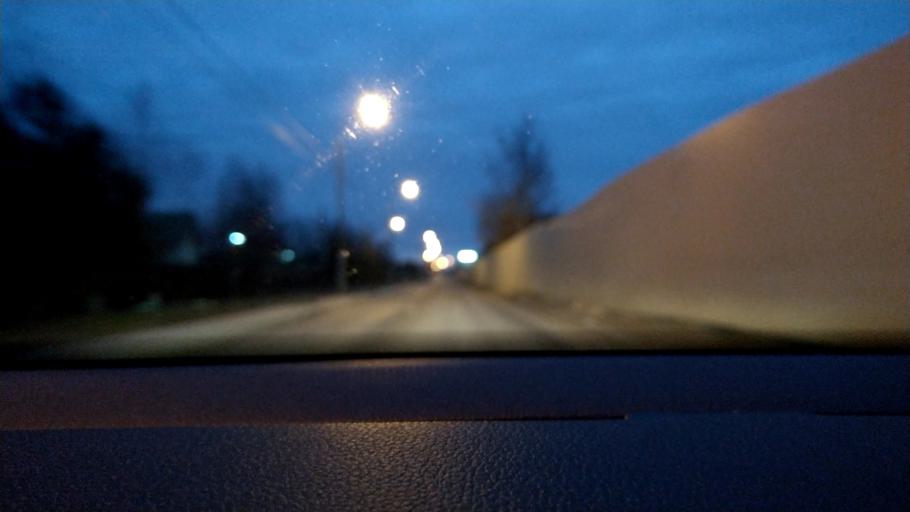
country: RU
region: Moscow
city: Tolstopal'tsevo
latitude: 55.6093
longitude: 37.1993
